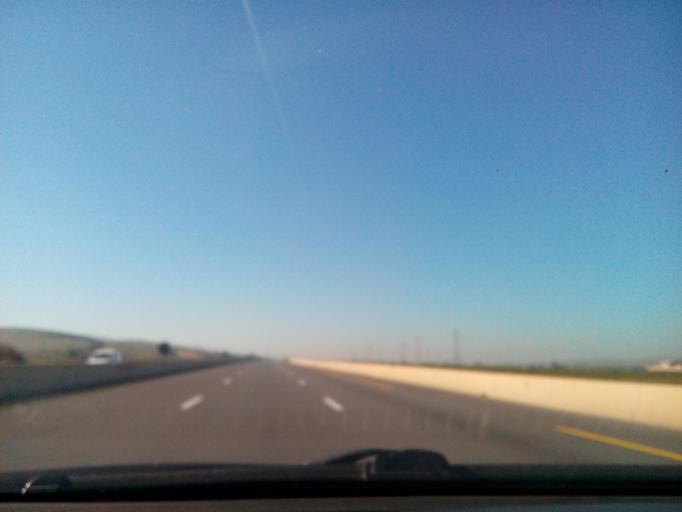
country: DZ
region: Chlef
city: Boukadir
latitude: 36.0395
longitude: 1.0898
